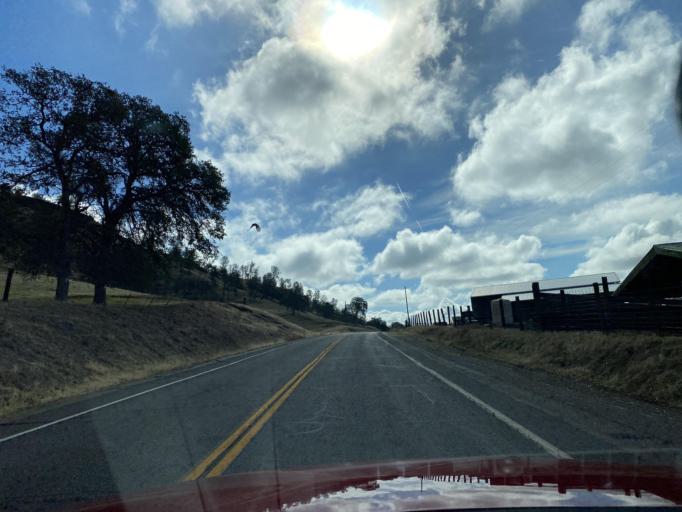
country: US
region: California
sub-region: Glenn County
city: Willows
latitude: 39.5562
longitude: -122.5413
